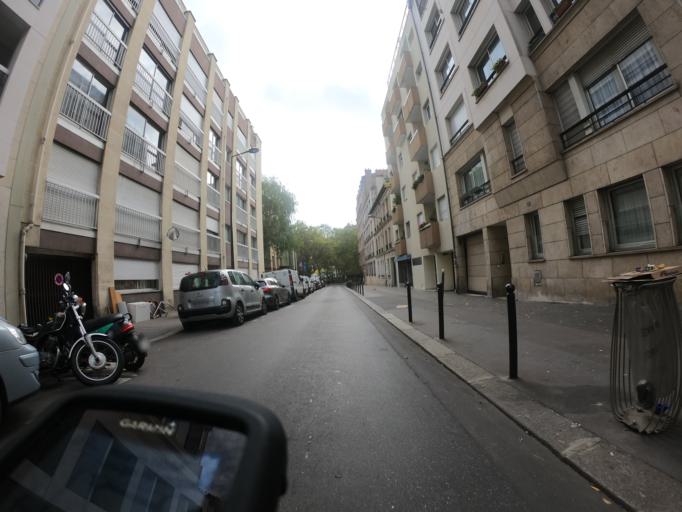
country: FR
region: Ile-de-France
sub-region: Departement du Val-de-Marne
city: Le Kremlin-Bicetre
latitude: 48.8245
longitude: 2.3523
